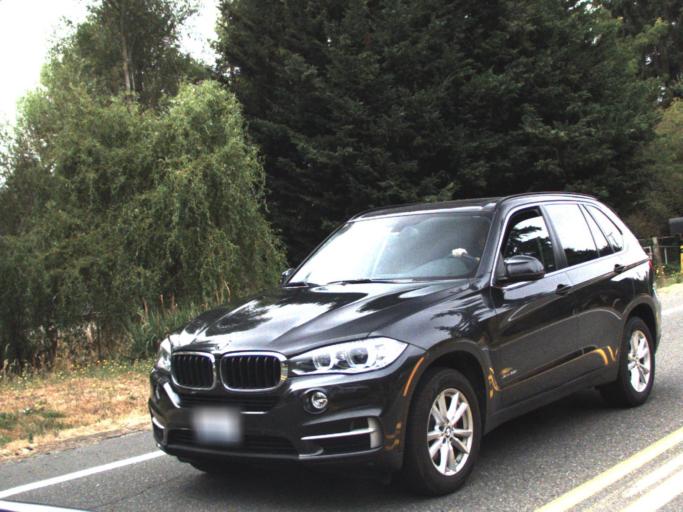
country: US
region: Washington
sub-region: King County
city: Woodinville
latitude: 47.7235
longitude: -122.1356
